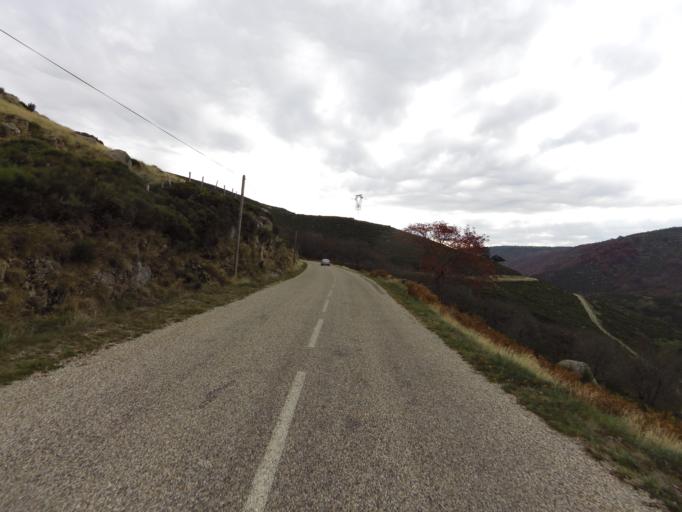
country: FR
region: Rhone-Alpes
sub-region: Departement de l'Ardeche
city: Les Vans
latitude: 44.5239
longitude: 4.0223
